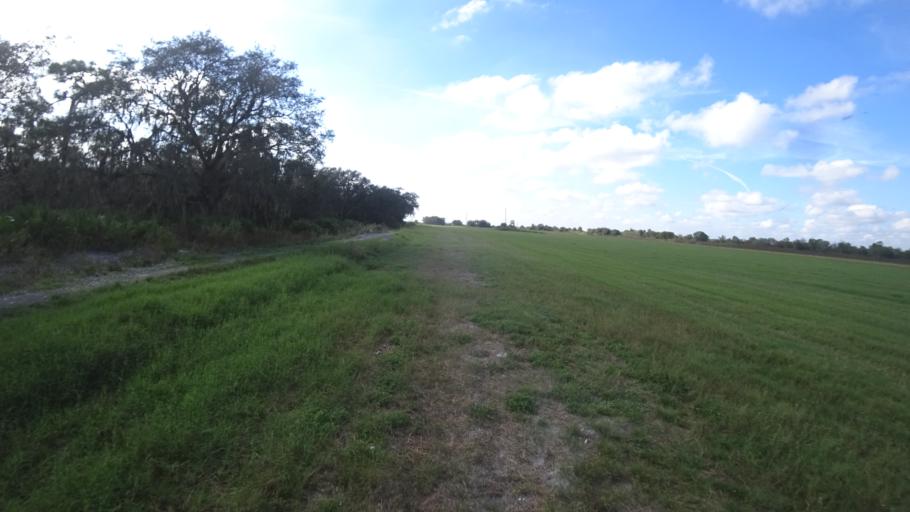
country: US
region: Florida
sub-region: Sarasota County
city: Lake Sarasota
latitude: 27.3728
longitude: -82.1658
